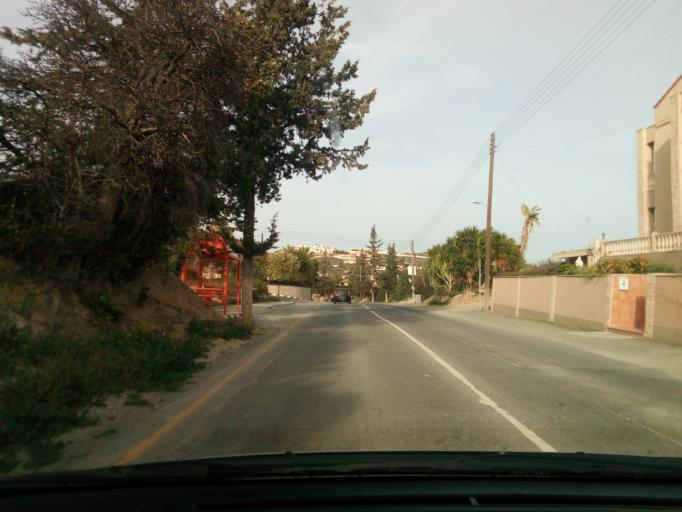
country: CY
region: Larnaka
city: Agios Tychon
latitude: 34.7158
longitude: 33.1292
